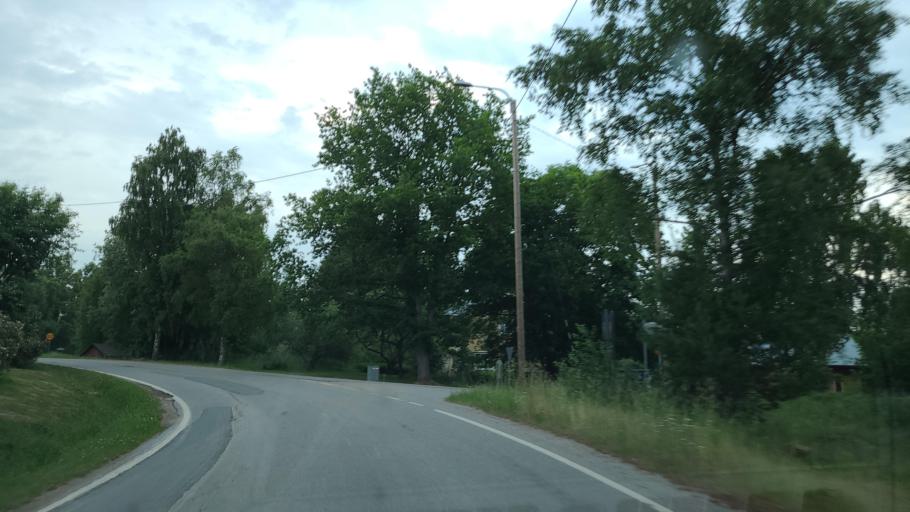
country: FI
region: Ostrobothnia
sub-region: Vaasa
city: Replot
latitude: 63.1803
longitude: 21.2816
